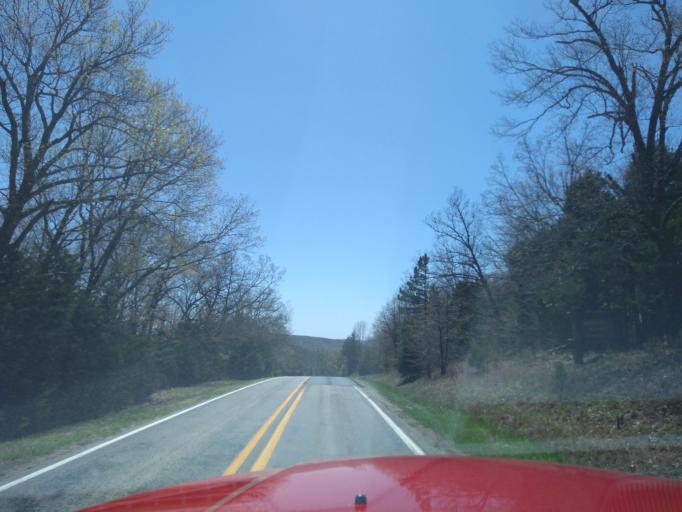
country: US
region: Arkansas
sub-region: Washington County
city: West Fork
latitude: 35.7951
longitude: -94.2549
